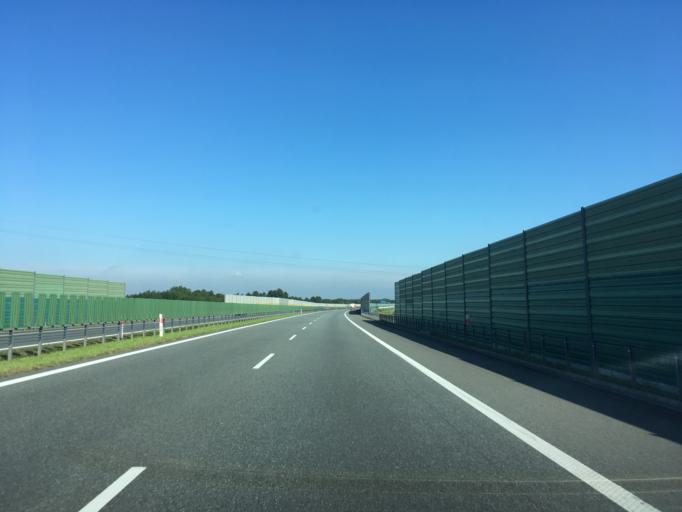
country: PL
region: Kujawsko-Pomorskie
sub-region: Powiat chelminski
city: Lisewo
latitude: 53.4022
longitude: 18.6842
